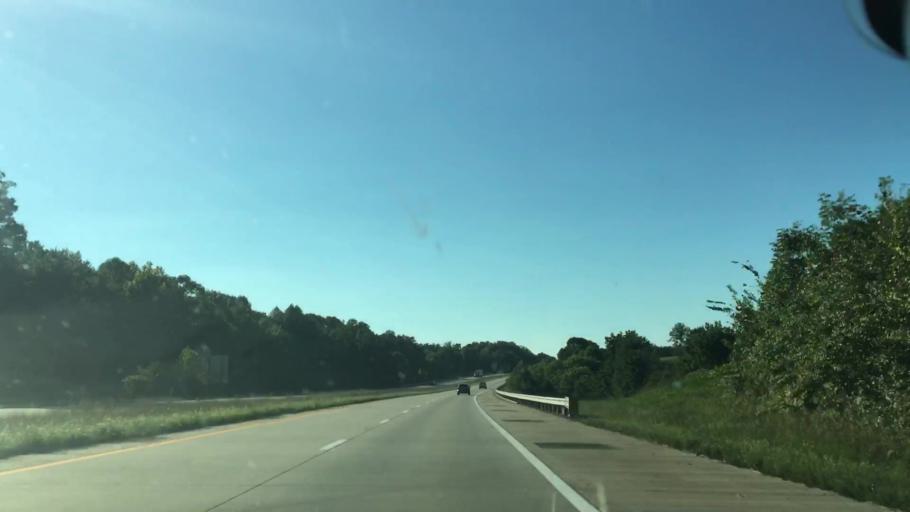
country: US
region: Indiana
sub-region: Warrick County
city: Newburgh
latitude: 37.7550
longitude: -87.4061
